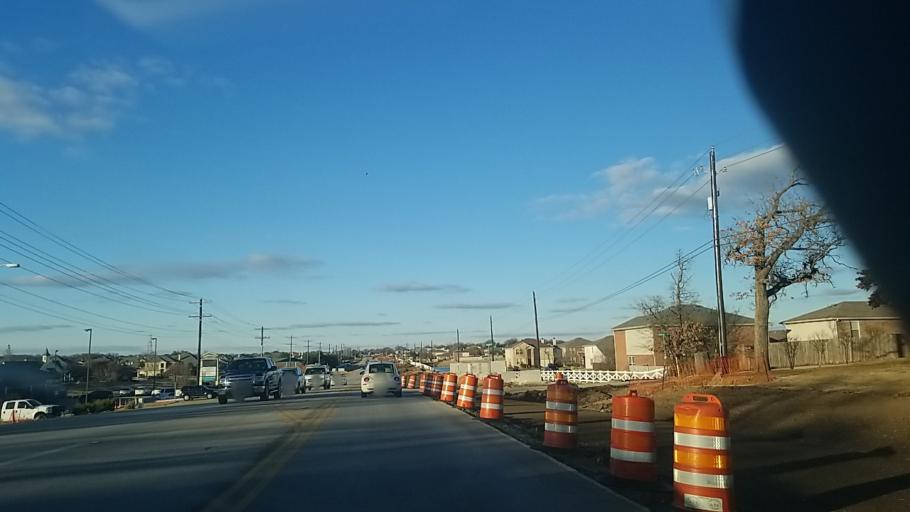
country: US
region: Texas
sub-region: Denton County
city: Corinth
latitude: 33.1500
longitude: -97.1053
